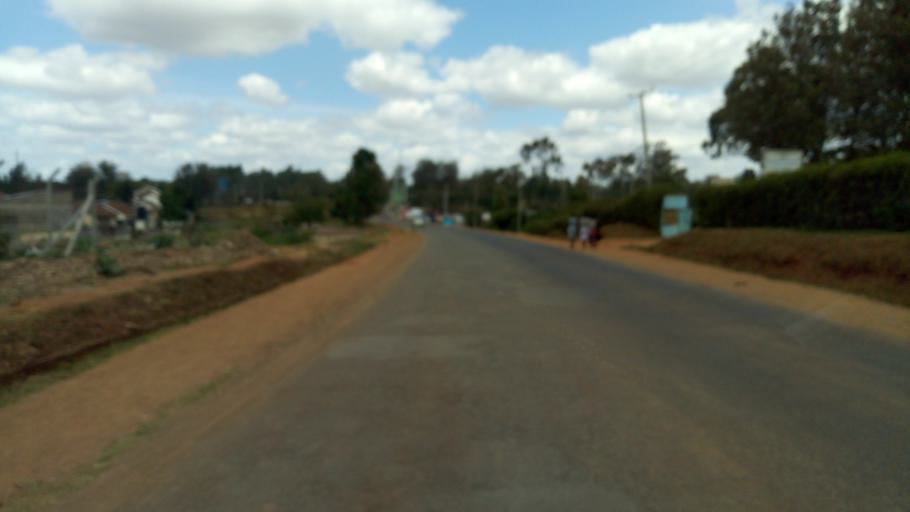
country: KE
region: Nairobi Area
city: Nairobi
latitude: -1.3278
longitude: 36.7801
